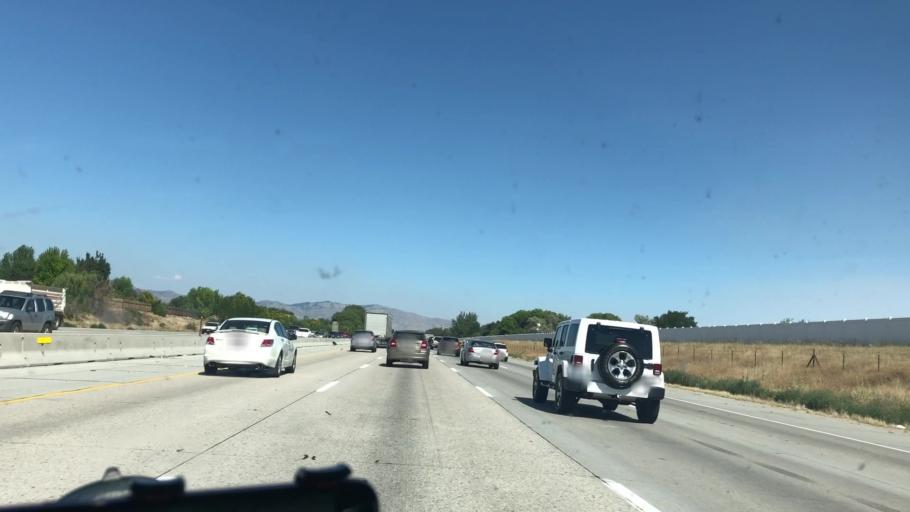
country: US
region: Idaho
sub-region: Ada County
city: Meridian
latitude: 43.5972
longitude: -116.3320
